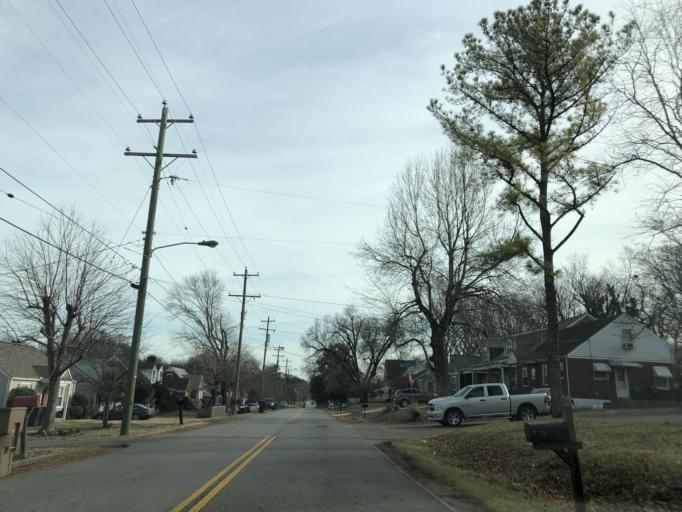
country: US
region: Tennessee
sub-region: Davidson County
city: Nashville
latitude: 36.2178
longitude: -86.7243
